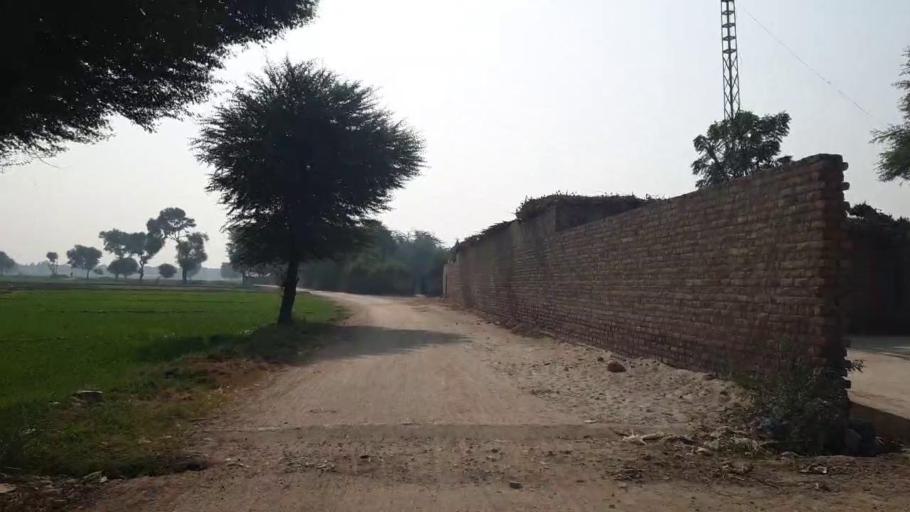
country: PK
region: Sindh
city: Kotri
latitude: 25.3563
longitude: 68.3081
